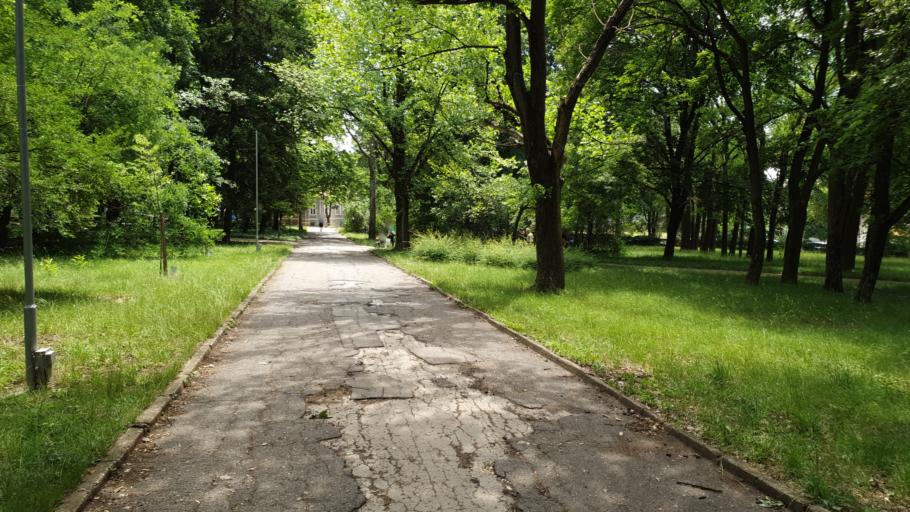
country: BG
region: Razgrad
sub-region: Obshtina Razgrad
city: Razgrad
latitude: 43.5313
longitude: 26.5304
